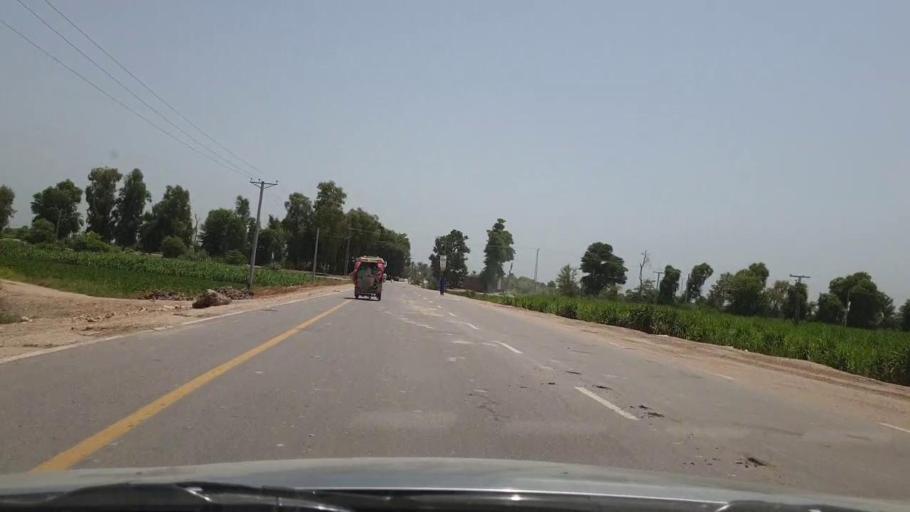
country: PK
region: Sindh
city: Pano Aqil
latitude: 27.8604
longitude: 69.0861
